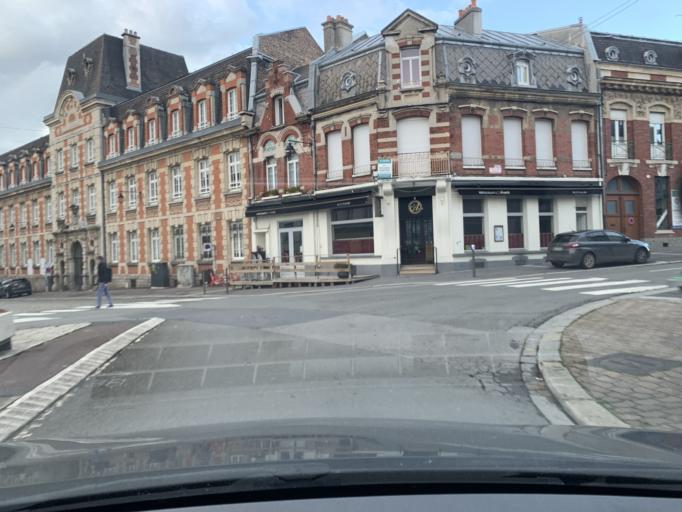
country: FR
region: Nord-Pas-de-Calais
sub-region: Departement du Nord
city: Cambrai
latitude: 50.1767
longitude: 3.2327
